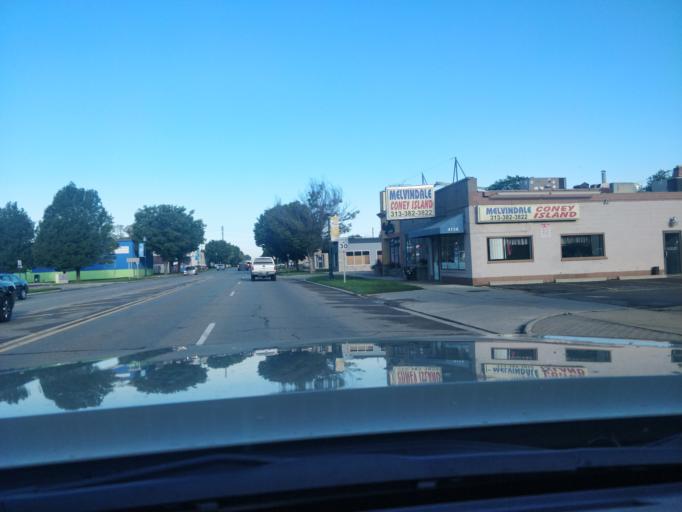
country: US
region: Michigan
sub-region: Wayne County
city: Melvindale
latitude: 42.2818
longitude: -83.1890
